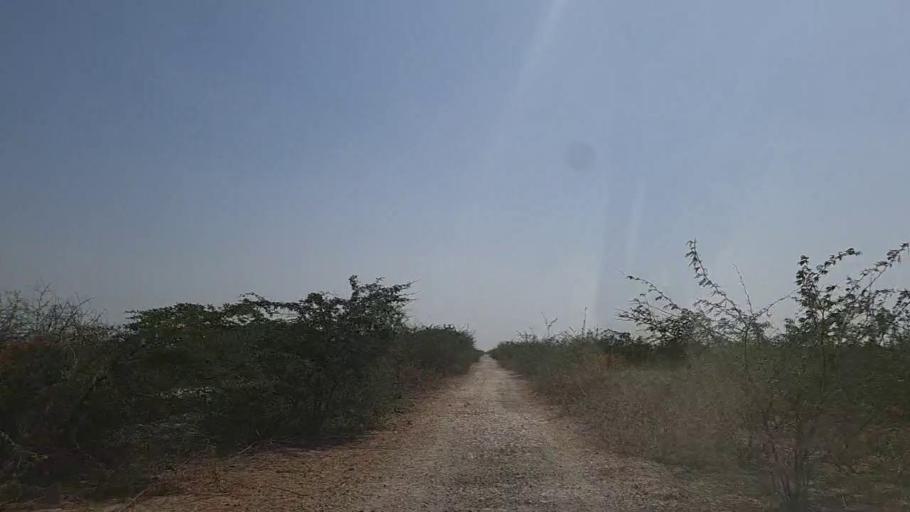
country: PK
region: Sindh
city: Naukot
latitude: 24.6444
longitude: 69.2752
